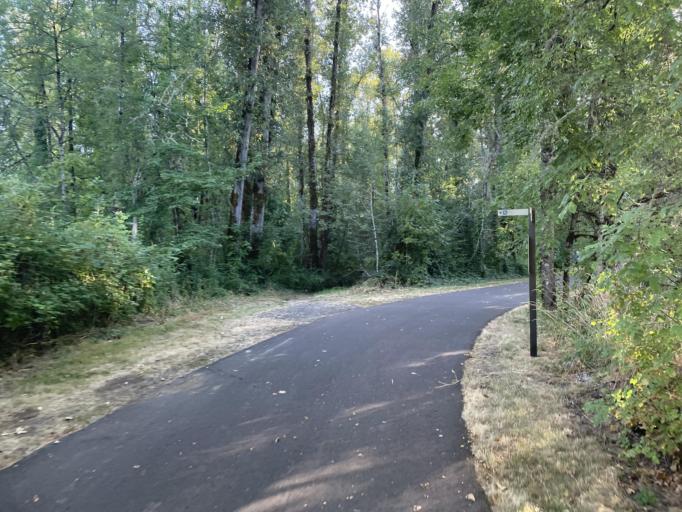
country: US
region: Oregon
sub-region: Marion County
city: Salem
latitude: 44.9172
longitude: -123.0787
